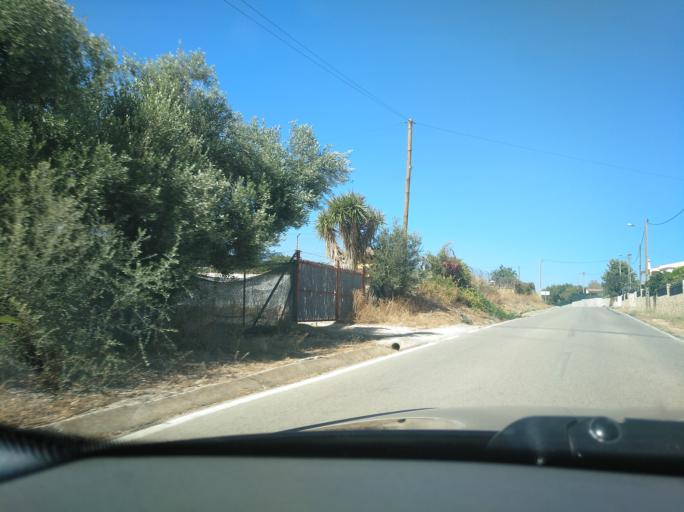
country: PT
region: Faro
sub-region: Faro
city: Faro
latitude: 37.0644
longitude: -7.8974
